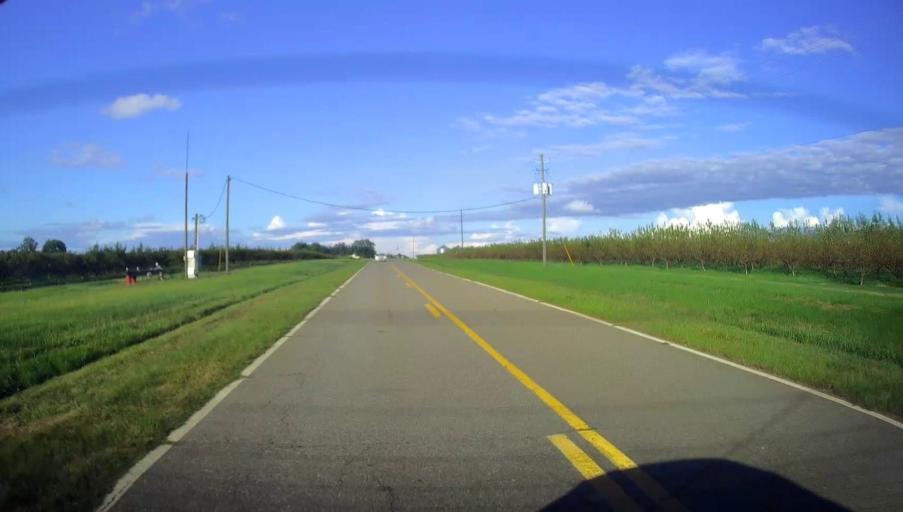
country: US
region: Georgia
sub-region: Bleckley County
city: Cochran
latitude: 32.3948
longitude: -83.4425
